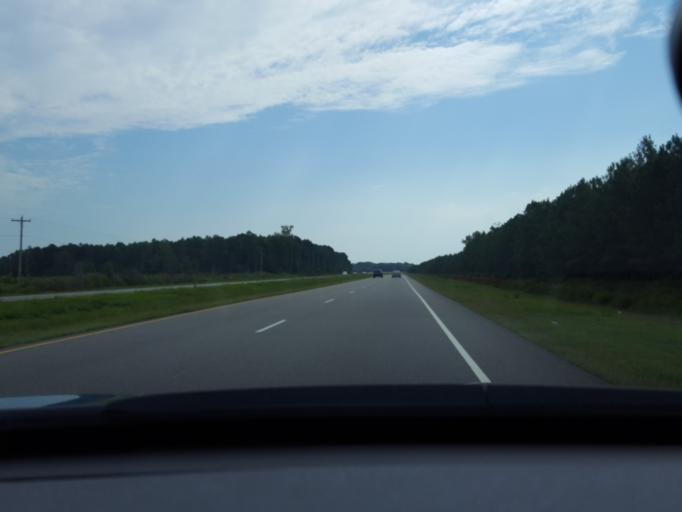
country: US
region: North Carolina
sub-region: Chowan County
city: Edenton
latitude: 36.0374
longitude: -76.7342
